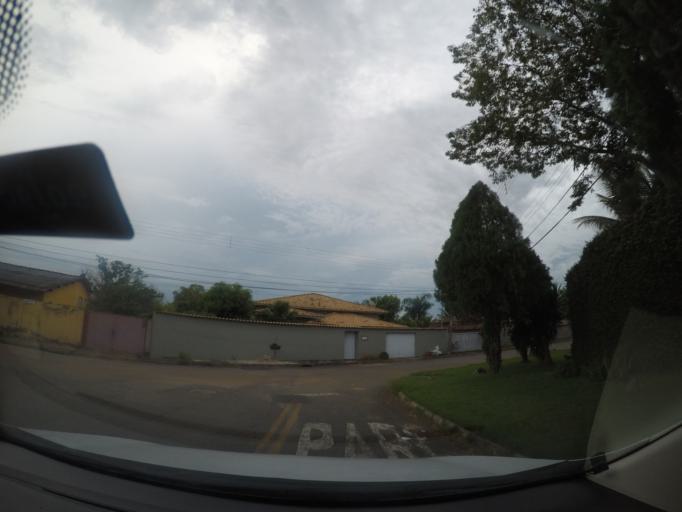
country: BR
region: Goias
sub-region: Goiania
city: Goiania
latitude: -16.6548
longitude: -49.2295
